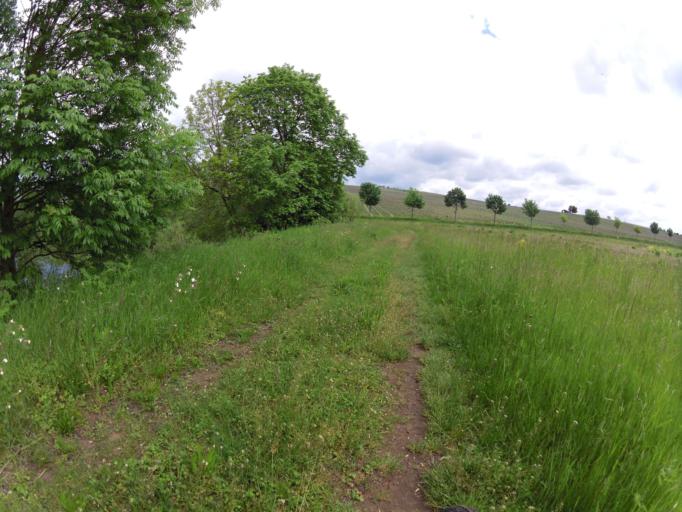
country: DE
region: Bavaria
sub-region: Regierungsbezirk Unterfranken
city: Sommerach
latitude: 49.8309
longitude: 10.1921
